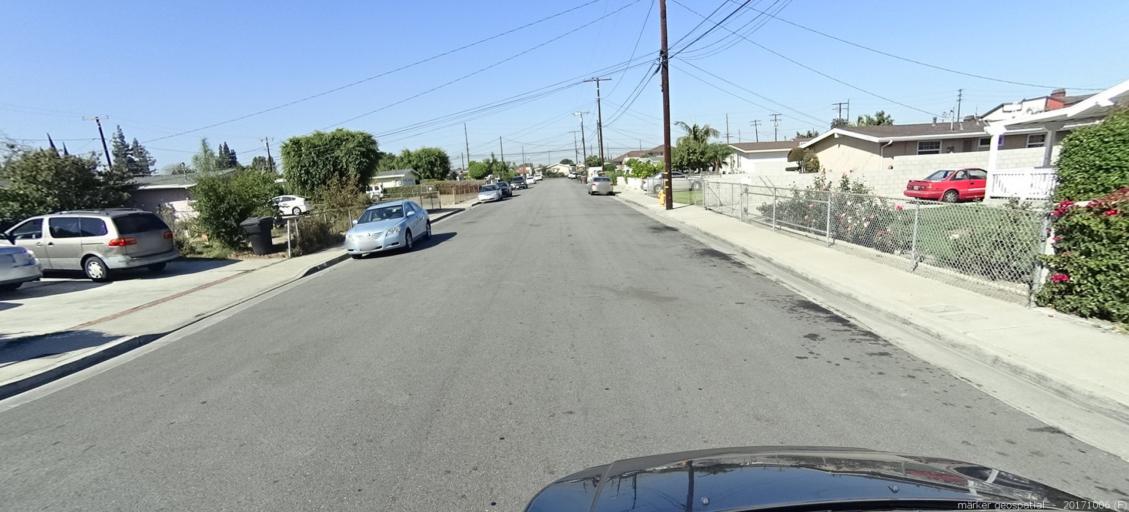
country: US
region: California
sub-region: Orange County
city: Stanton
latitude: 33.7871
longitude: -117.9823
